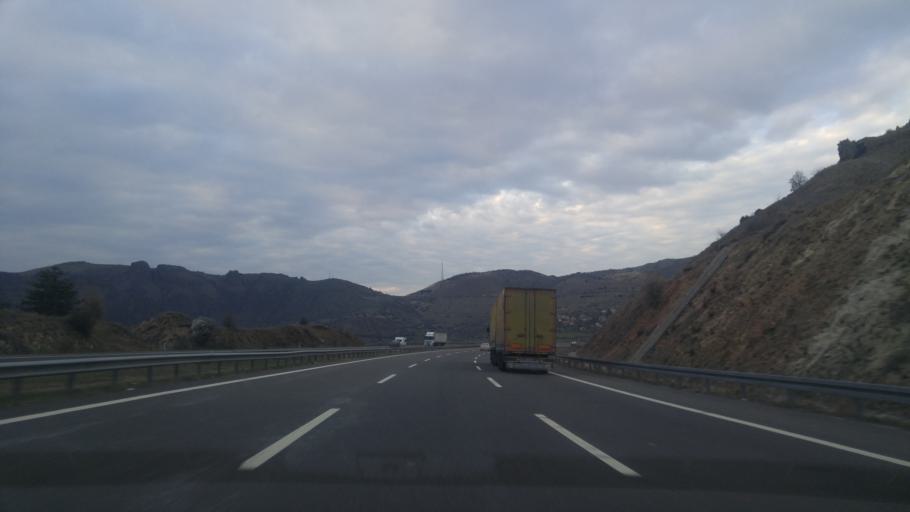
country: TR
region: Ankara
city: Celtikci
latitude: 40.3614
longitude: 32.4650
